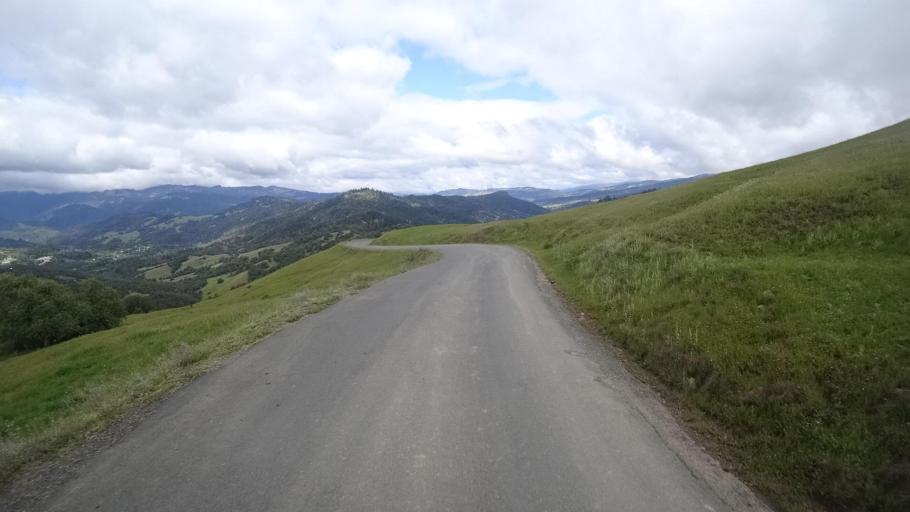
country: US
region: California
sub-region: Humboldt County
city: Redway
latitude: 40.1768
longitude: -123.5713
